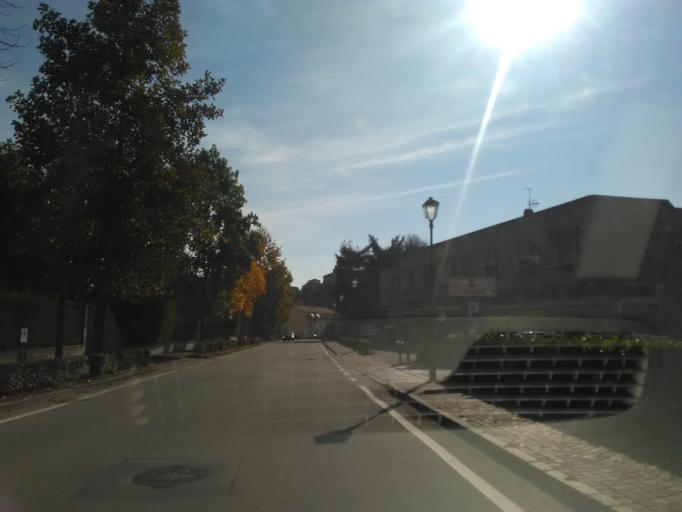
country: IT
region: Piedmont
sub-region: Provincia di Vercelli
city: Borgosesia
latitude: 45.7147
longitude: 8.2840
